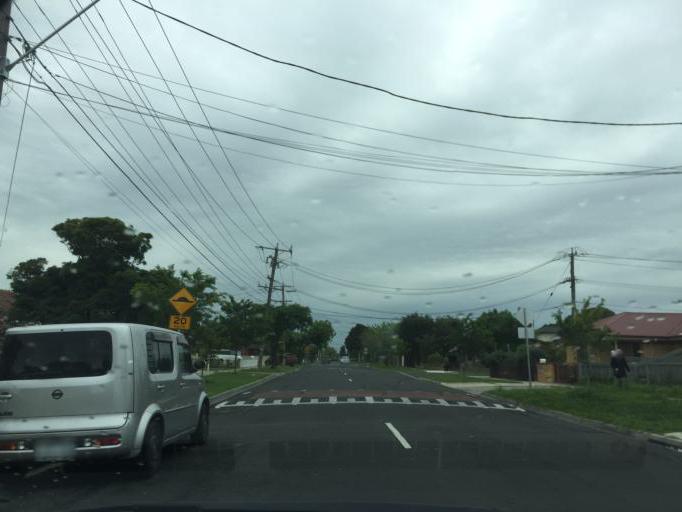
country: AU
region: Victoria
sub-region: Maribyrnong
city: Braybrook
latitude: -37.7817
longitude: 144.8516
